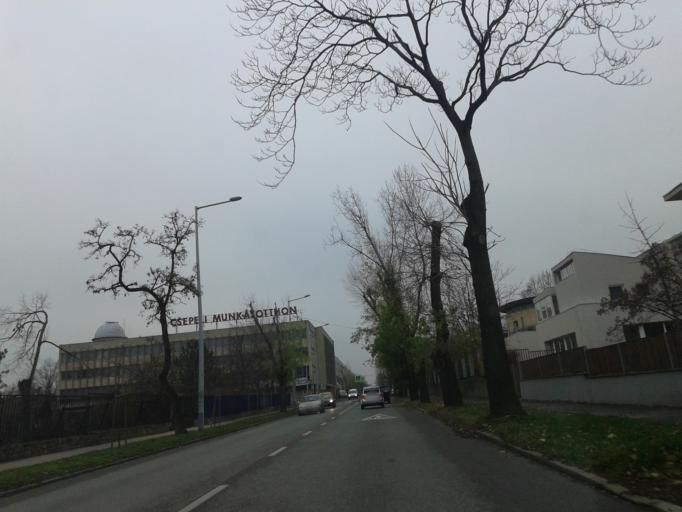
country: HU
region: Budapest
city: Budapest XXI. keruelet
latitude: 47.4337
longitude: 19.0728
